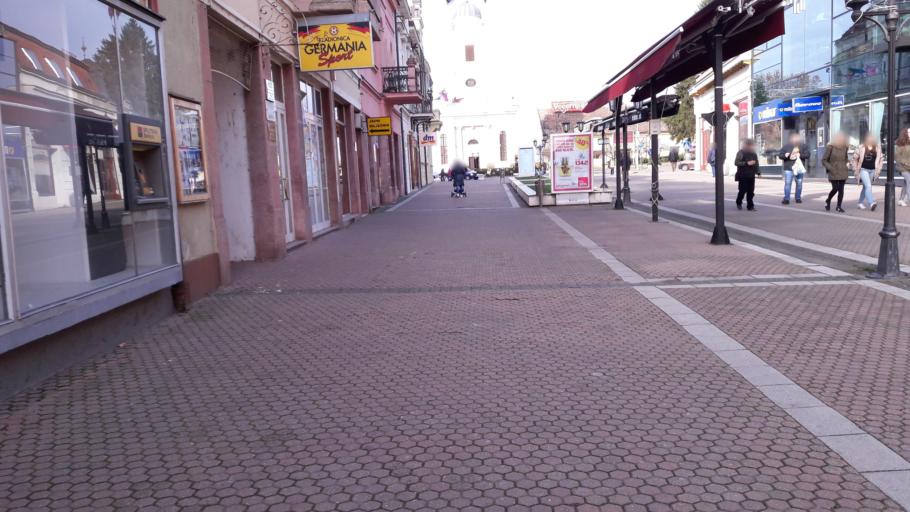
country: HR
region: Osjecko-Baranjska
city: Piskorevci
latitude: 45.3093
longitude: 18.4104
